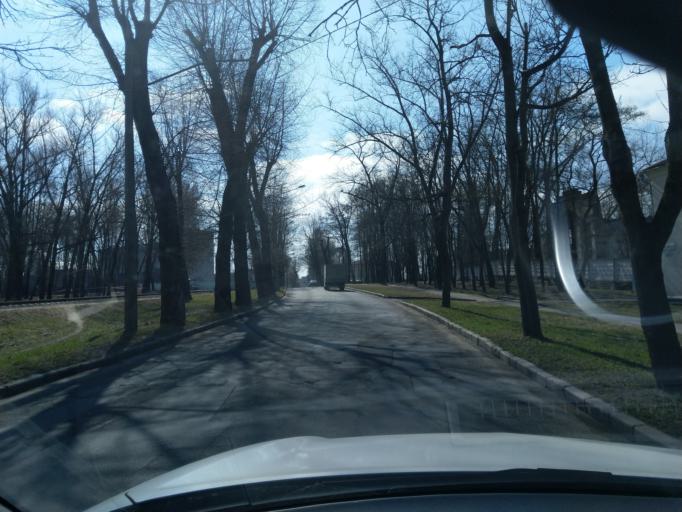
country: BY
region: Minsk
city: Syenitsa
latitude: 53.8744
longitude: 27.5113
